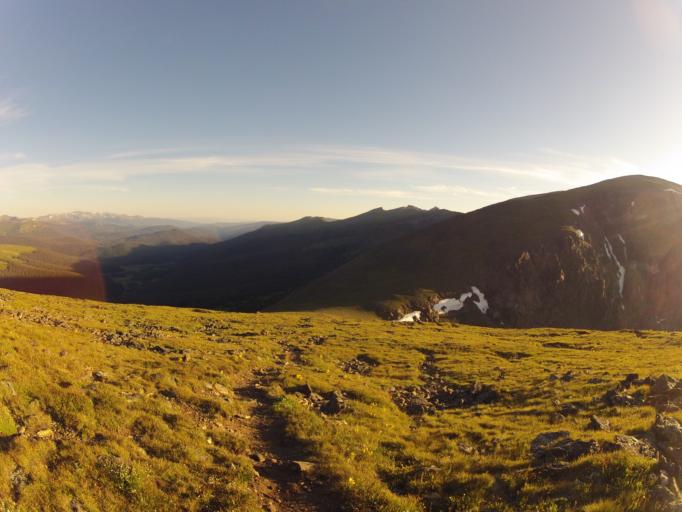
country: US
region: Colorado
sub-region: Larimer County
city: Estes Park
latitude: 40.4352
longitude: -105.7020
